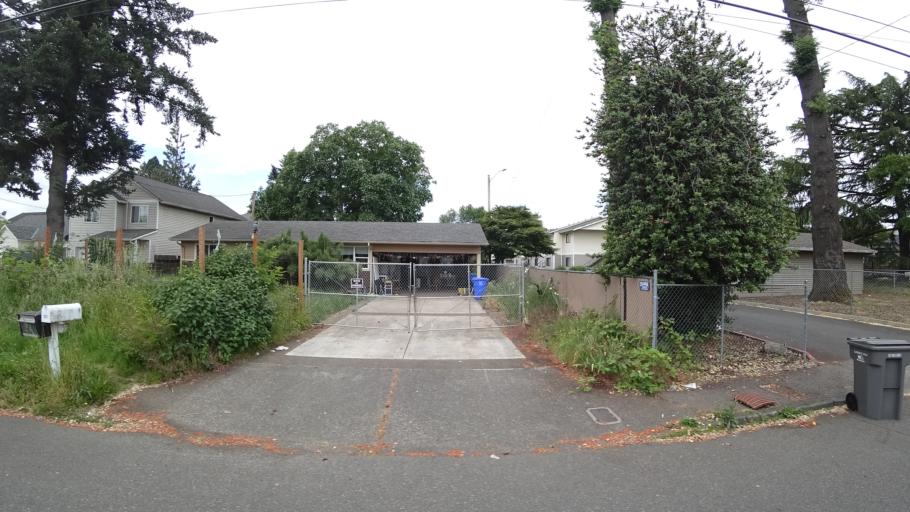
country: US
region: Oregon
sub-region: Multnomah County
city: Lents
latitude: 45.5020
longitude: -122.5348
